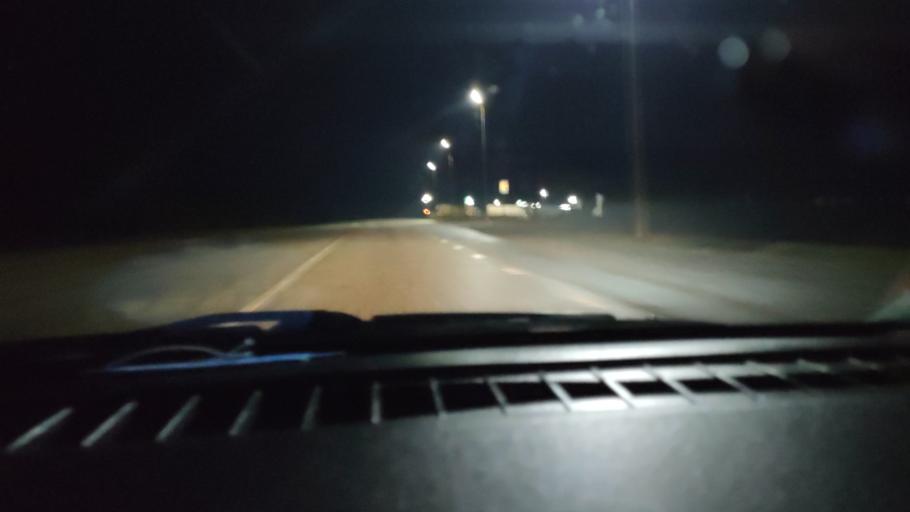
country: RU
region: Tatarstan
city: Agryz
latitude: 56.4778
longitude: 52.7986
